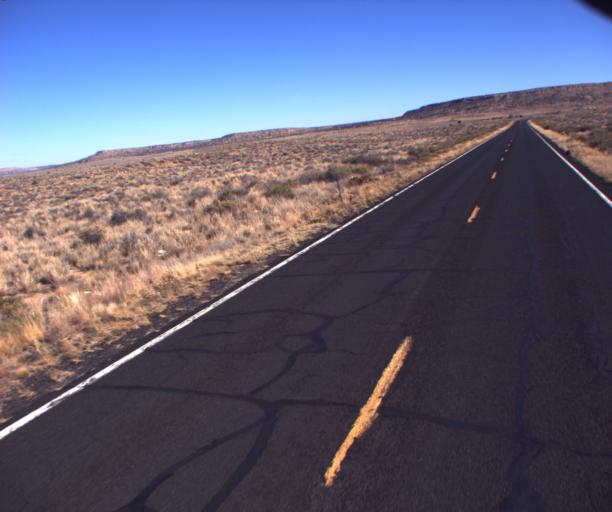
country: US
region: Arizona
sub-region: Navajo County
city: First Mesa
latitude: 35.8416
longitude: -110.3321
